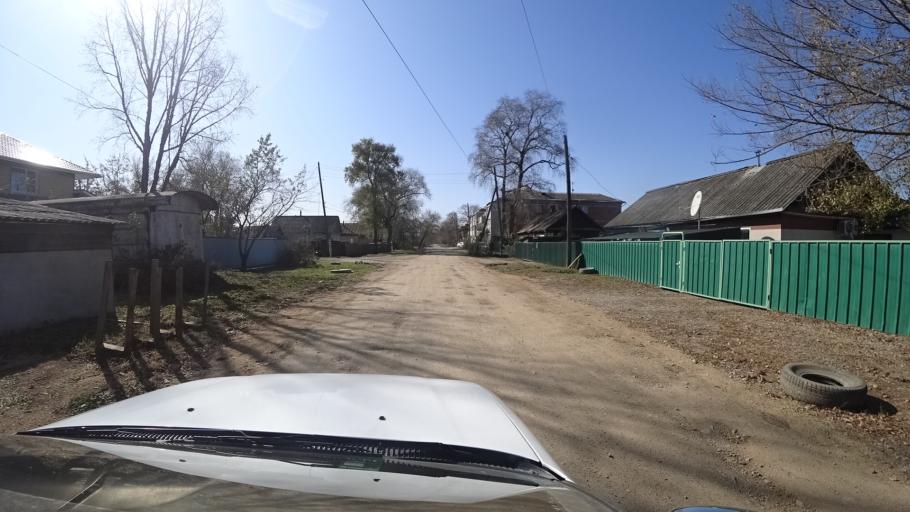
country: RU
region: Primorskiy
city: Dal'nerechensk
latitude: 45.9317
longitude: 133.7469
